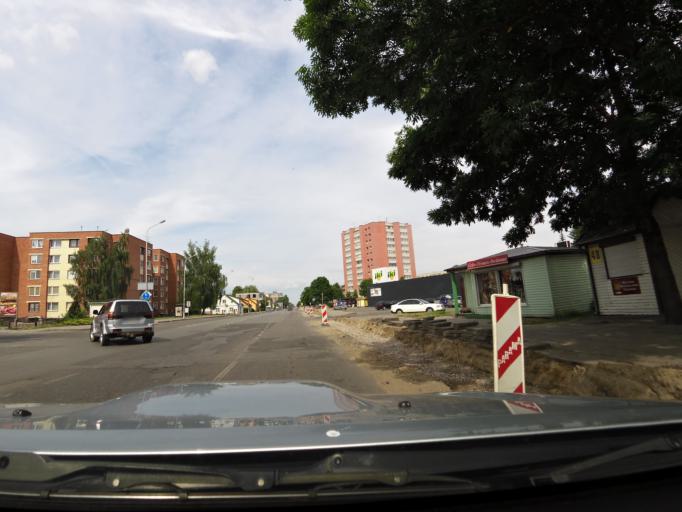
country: LT
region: Marijampoles apskritis
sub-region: Marijampole Municipality
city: Marijampole
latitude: 54.5631
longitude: 23.3545
